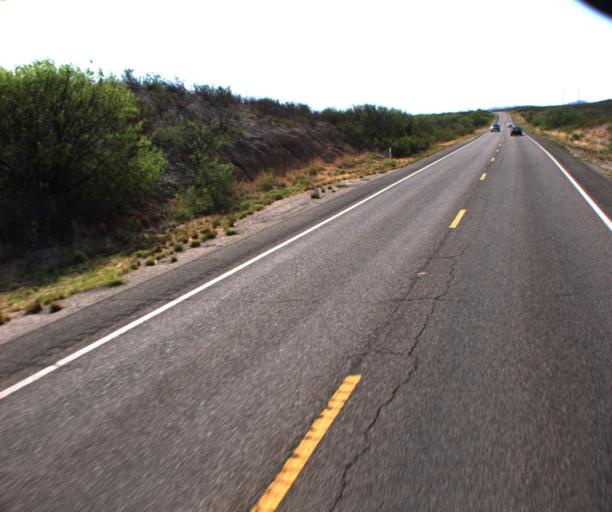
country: US
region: Arizona
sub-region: Cochise County
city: Tombstone
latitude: 31.7904
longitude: -110.1504
